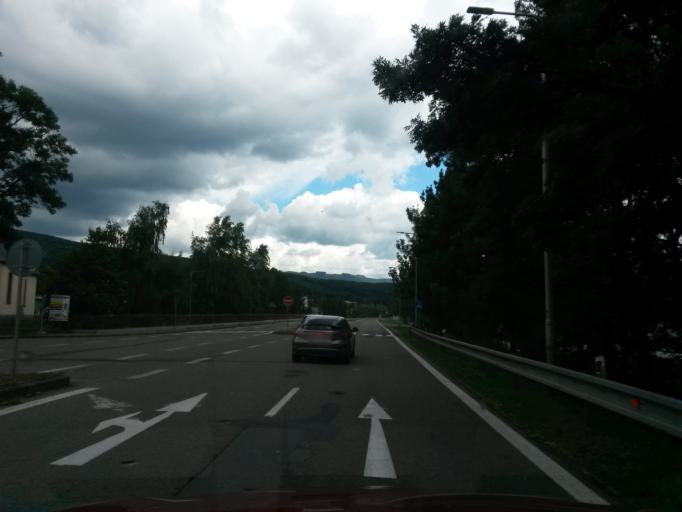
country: SK
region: Kosicky
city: Vinne
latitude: 48.8049
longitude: 22.0029
